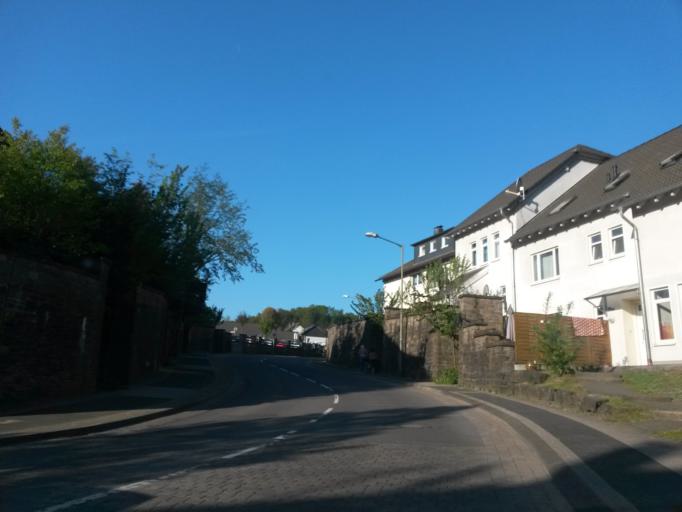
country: DE
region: North Rhine-Westphalia
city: Wiehl
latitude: 50.9632
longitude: 7.5058
